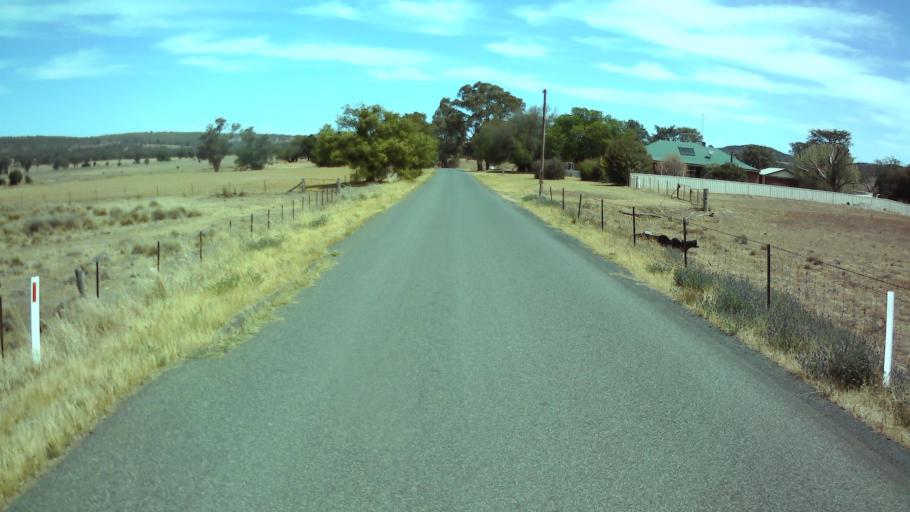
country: AU
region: New South Wales
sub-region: Weddin
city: Grenfell
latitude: -33.8330
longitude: 148.1740
